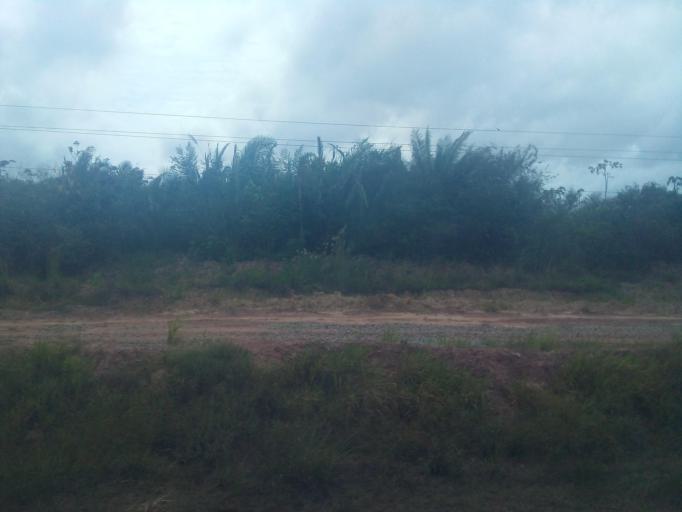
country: BR
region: Maranhao
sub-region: Itapecuru Mirim
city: Itapecuru Mirim
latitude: -3.1698
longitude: -44.3618
